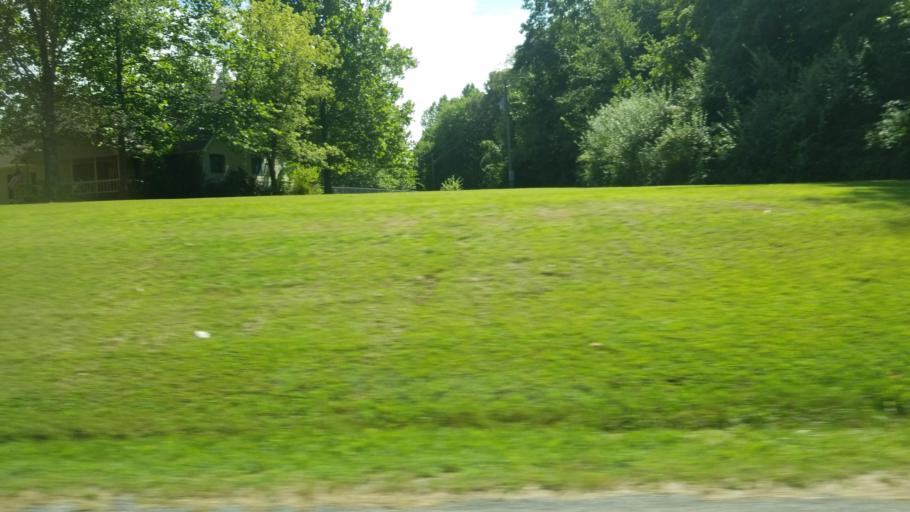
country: US
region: Illinois
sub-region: Williamson County
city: Johnston City
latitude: 37.7903
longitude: -88.8353
